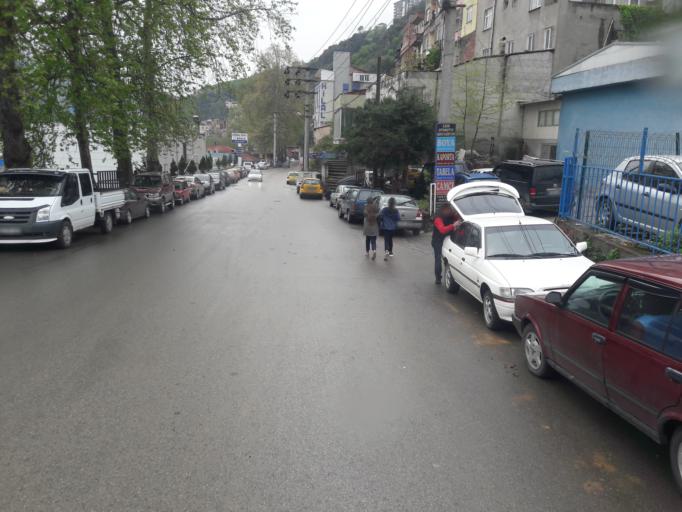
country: TR
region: Trabzon
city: Trabzon
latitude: 40.9921
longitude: 39.7489
